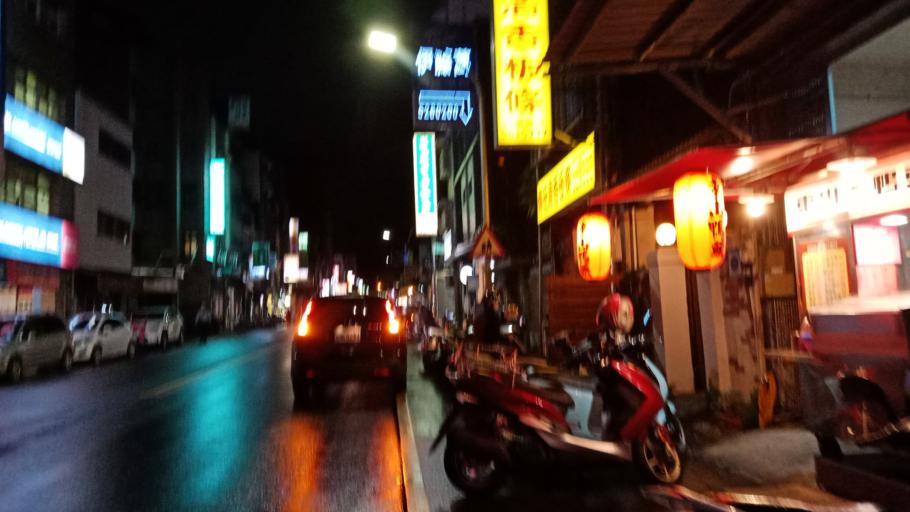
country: TW
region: Taiwan
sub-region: Hsinchu
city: Hsinchu
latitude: 24.7977
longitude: 120.9741
